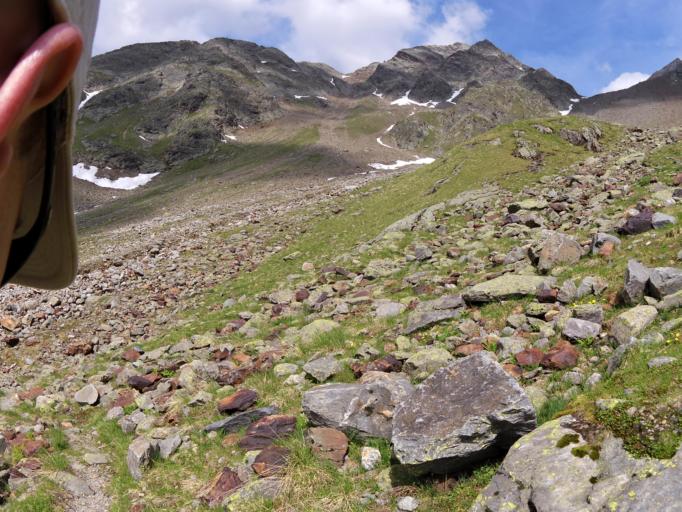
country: AT
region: Tyrol
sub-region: Politischer Bezirk Innsbruck Land
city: Gschnitz
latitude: 47.0323
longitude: 11.2939
